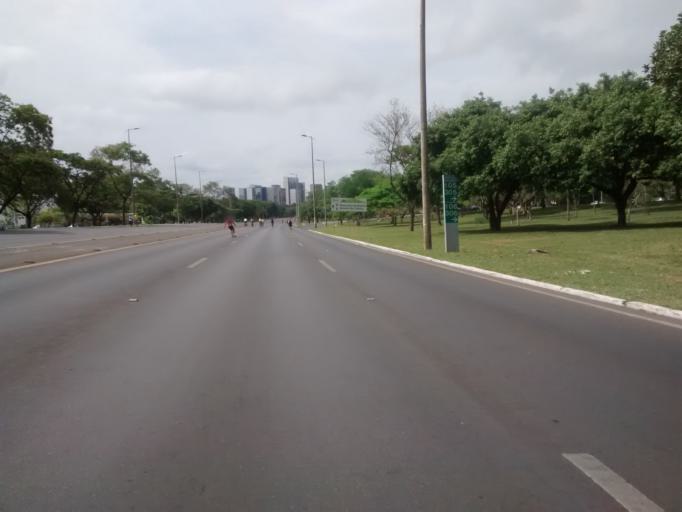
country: BR
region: Federal District
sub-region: Brasilia
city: Brasilia
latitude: -15.7730
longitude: -47.8814
